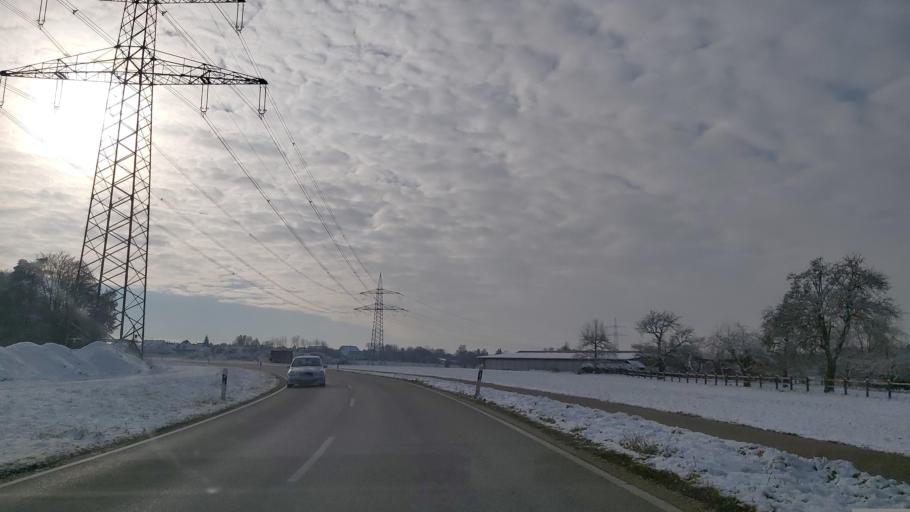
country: DE
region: Bavaria
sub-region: Swabia
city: Senden
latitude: 48.3434
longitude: 10.0710
